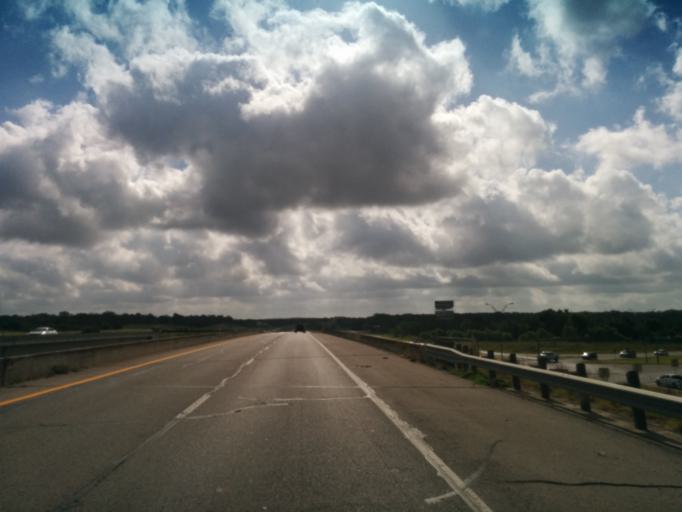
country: US
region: Texas
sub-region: Caldwell County
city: Luling
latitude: 29.6522
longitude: -97.5934
